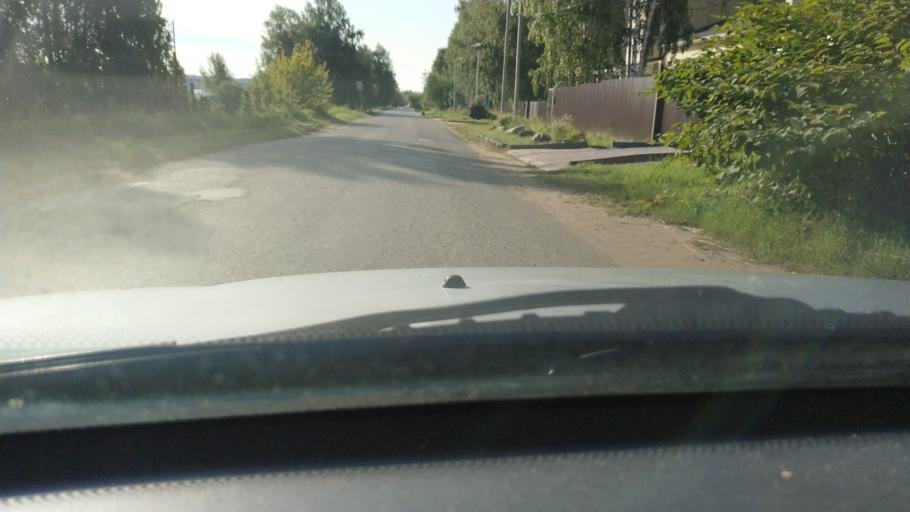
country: RU
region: Kostroma
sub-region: Kostromskoy Rayon
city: Kostroma
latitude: 57.7543
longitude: 40.9205
